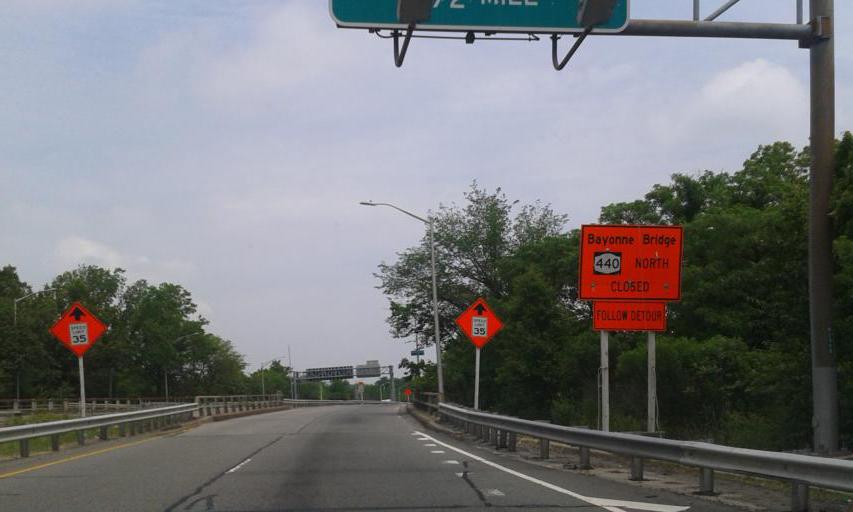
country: US
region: New York
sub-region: Richmond County
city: Bloomfield
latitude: 40.6169
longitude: -74.1523
